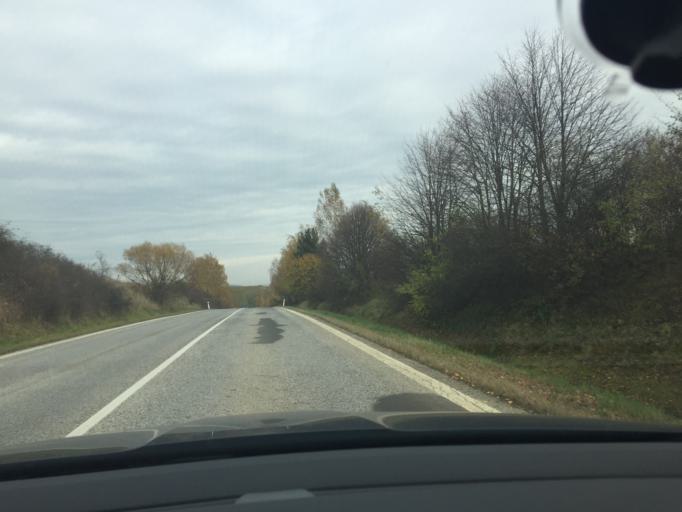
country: SK
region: Presovsky
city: Sabinov
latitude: 49.0038
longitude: 21.1121
